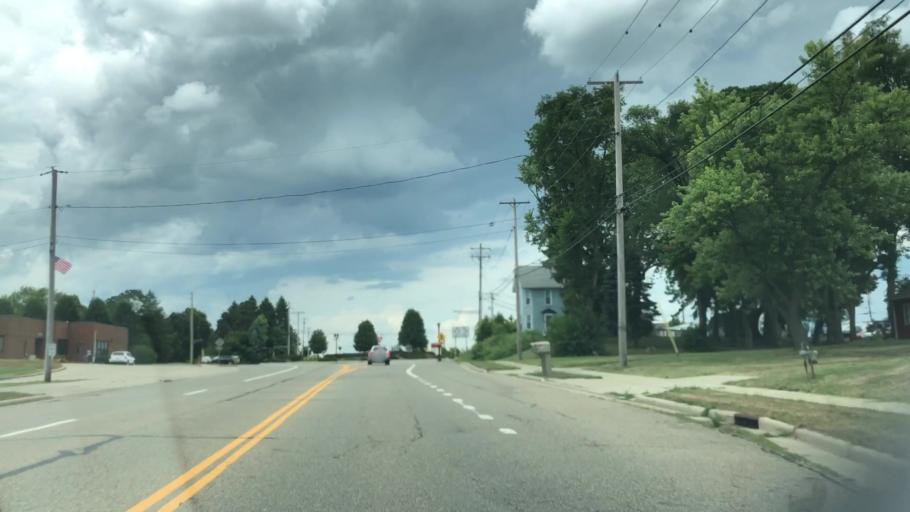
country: US
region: Ohio
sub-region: Summit County
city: Greensburg
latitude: 40.9464
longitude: -81.4652
